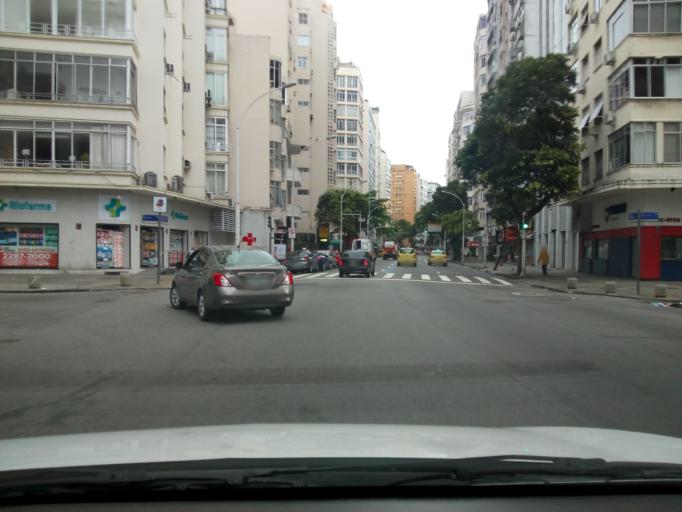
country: BR
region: Rio de Janeiro
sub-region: Rio De Janeiro
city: Rio de Janeiro
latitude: -22.9820
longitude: -43.1911
